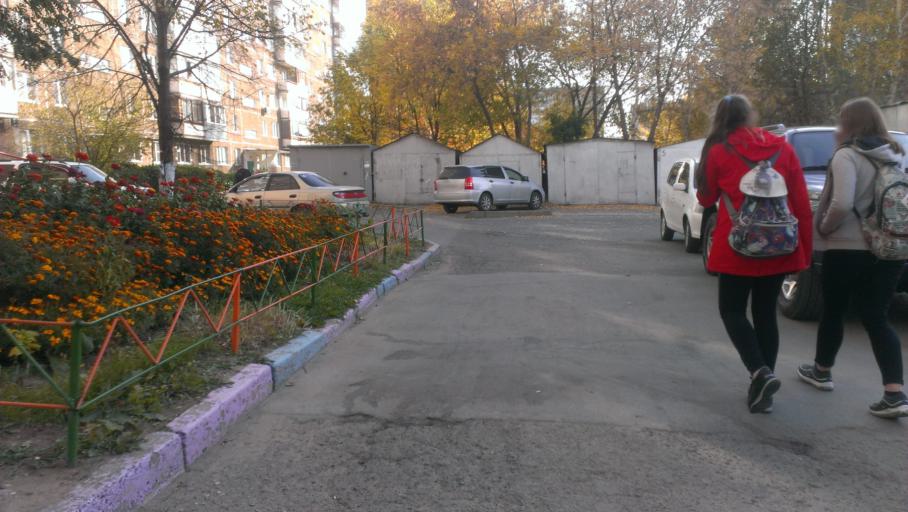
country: RU
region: Altai Krai
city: Novosilikatnyy
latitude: 53.3333
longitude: 83.6758
